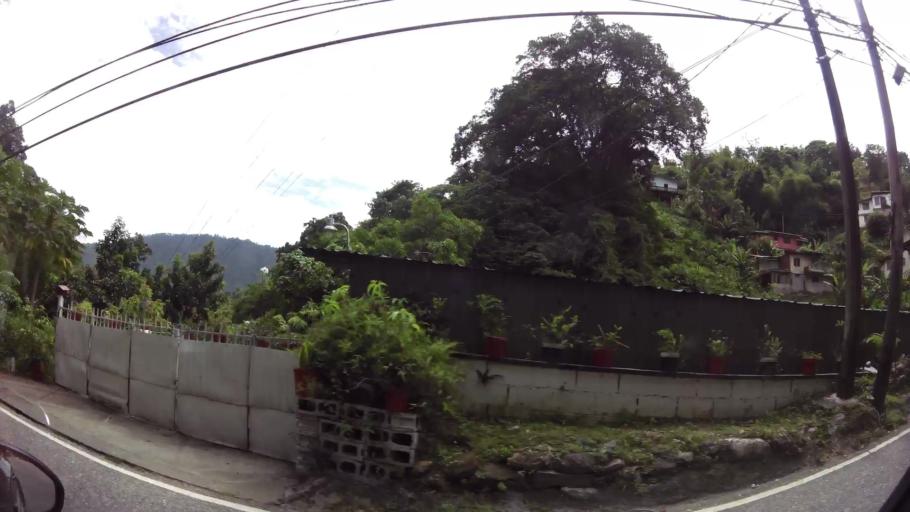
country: TT
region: Diego Martin
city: Petit Valley
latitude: 10.7161
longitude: -61.5223
